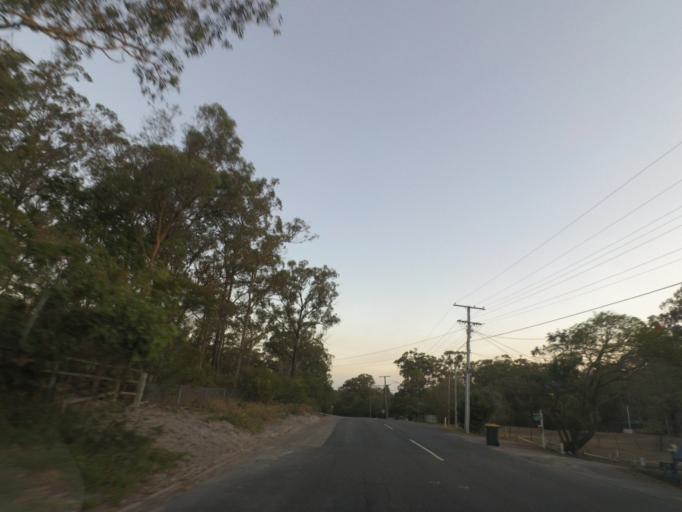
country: AU
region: Queensland
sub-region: Brisbane
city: Mackenzie
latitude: -27.5477
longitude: 153.1242
